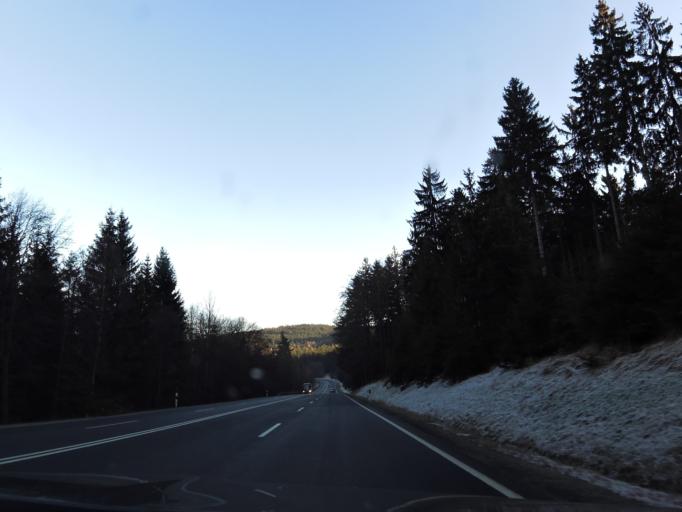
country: DE
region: Bavaria
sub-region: Upper Franconia
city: Nagel
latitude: 50.0044
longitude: 11.9088
